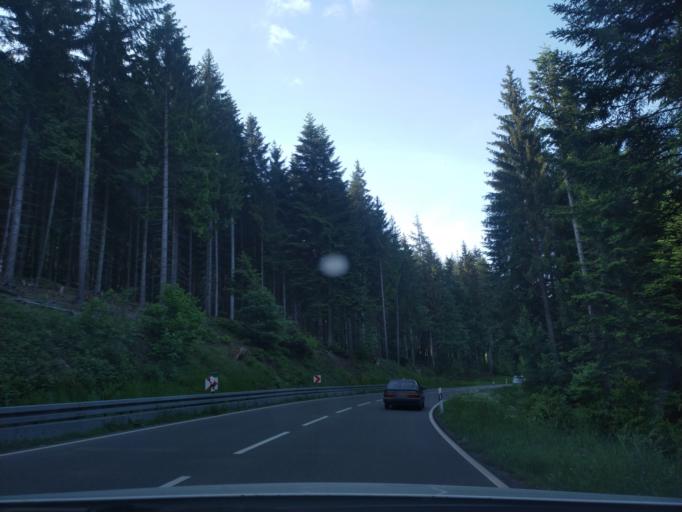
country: DE
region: Baden-Wuerttemberg
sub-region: Karlsruhe Region
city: Lossburg
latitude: 48.4303
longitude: 8.4404
